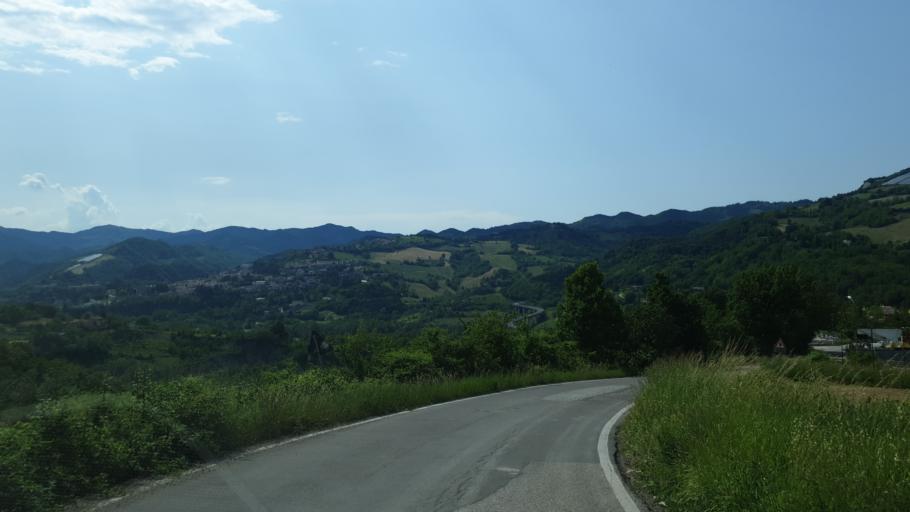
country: IT
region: Emilia-Romagna
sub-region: Forli-Cesena
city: Sarsina
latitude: 43.9188
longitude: 12.1667
